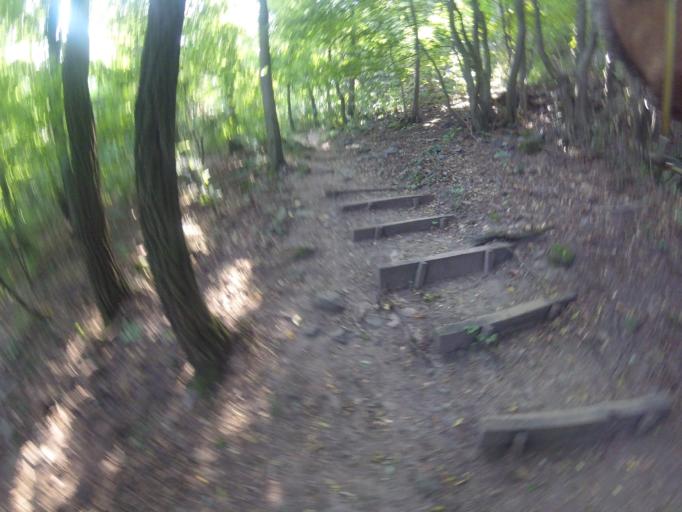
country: HU
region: Veszprem
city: Badacsonytomaj
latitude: 46.8071
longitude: 17.4958
